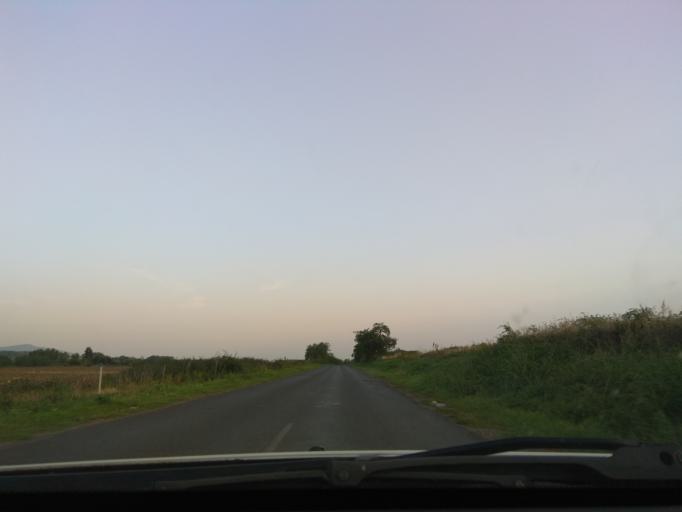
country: HU
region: Borsod-Abauj-Zemplen
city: Tallya
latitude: 48.2015
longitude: 21.2124
